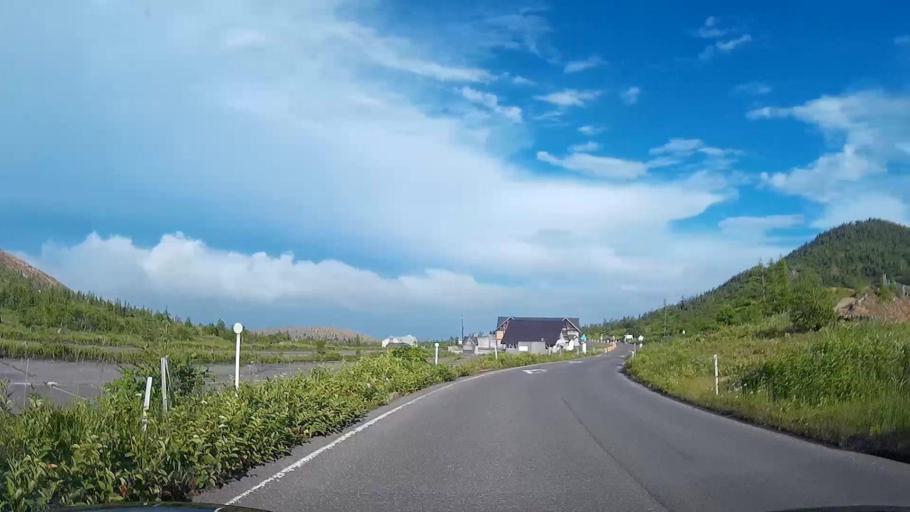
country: JP
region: Nagano
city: Nakano
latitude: 36.6382
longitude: 138.5322
